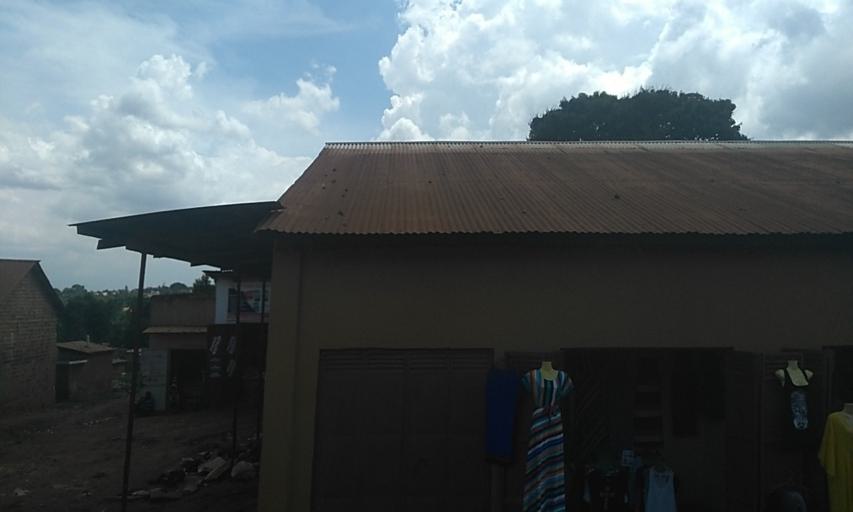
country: UG
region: Central Region
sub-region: Wakiso District
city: Wakiso
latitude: 0.3991
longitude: 32.4831
